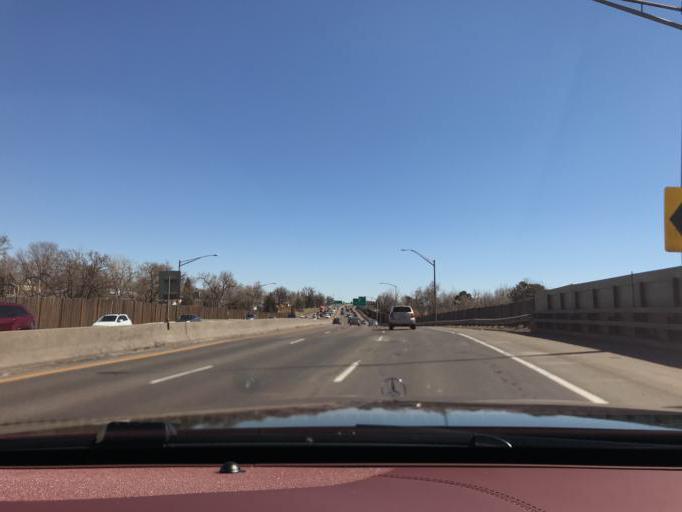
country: US
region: Colorado
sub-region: Adams County
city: Berkley
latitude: 39.7836
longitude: -105.0446
